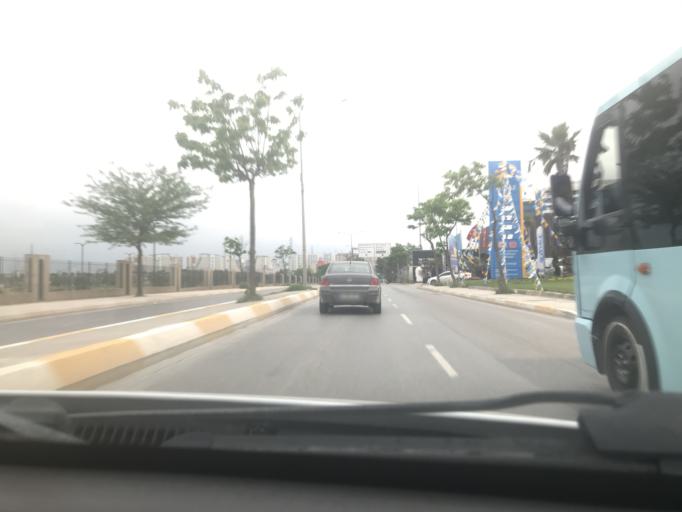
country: TR
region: Istanbul
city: Sultanbeyli
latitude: 40.9263
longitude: 29.3162
